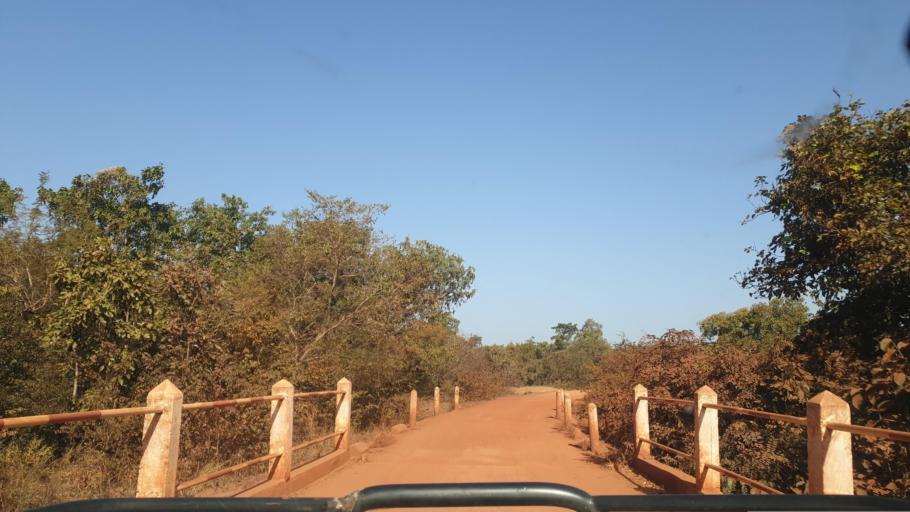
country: ML
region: Sikasso
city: Bougouni
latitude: 11.7783
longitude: -6.9075
